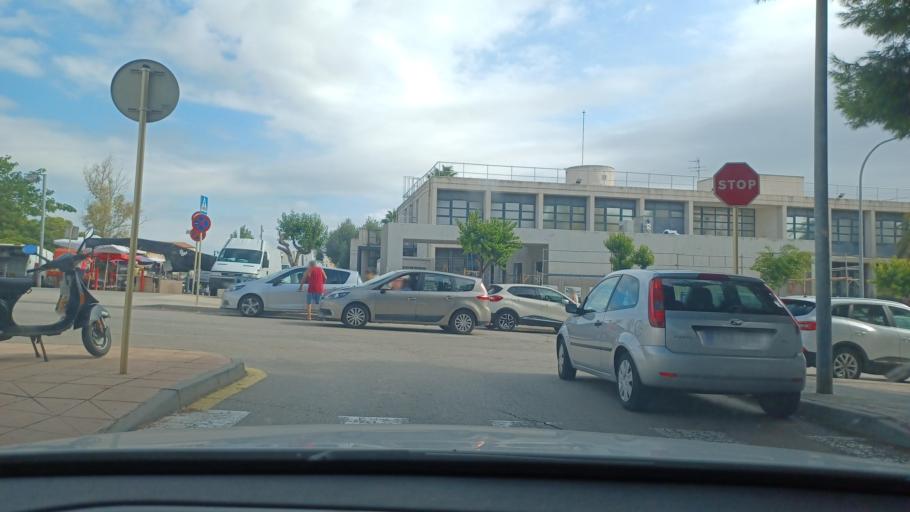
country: ES
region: Catalonia
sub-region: Provincia de Tarragona
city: Sant Carles de la Rapita
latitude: 40.6188
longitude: 0.5865
